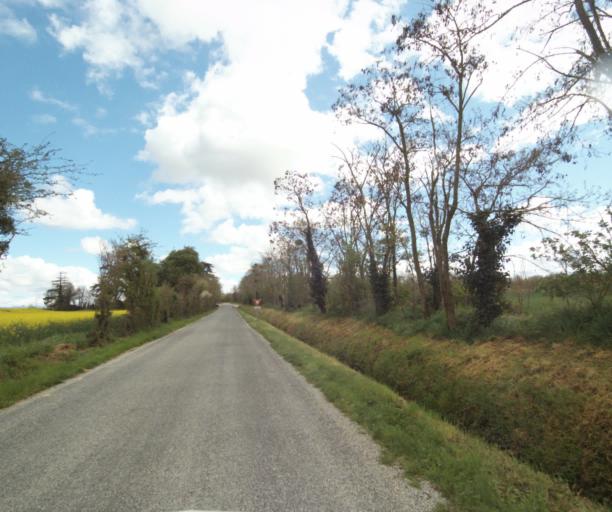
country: FR
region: Midi-Pyrenees
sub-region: Departement de l'Ariege
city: Mazeres
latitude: 43.2375
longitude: 1.6330
